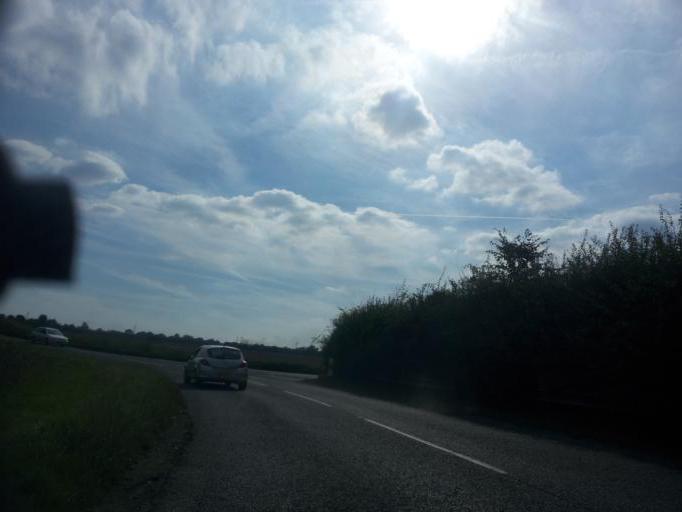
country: GB
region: England
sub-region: Kent
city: Boxley
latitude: 51.3392
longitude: 0.5635
